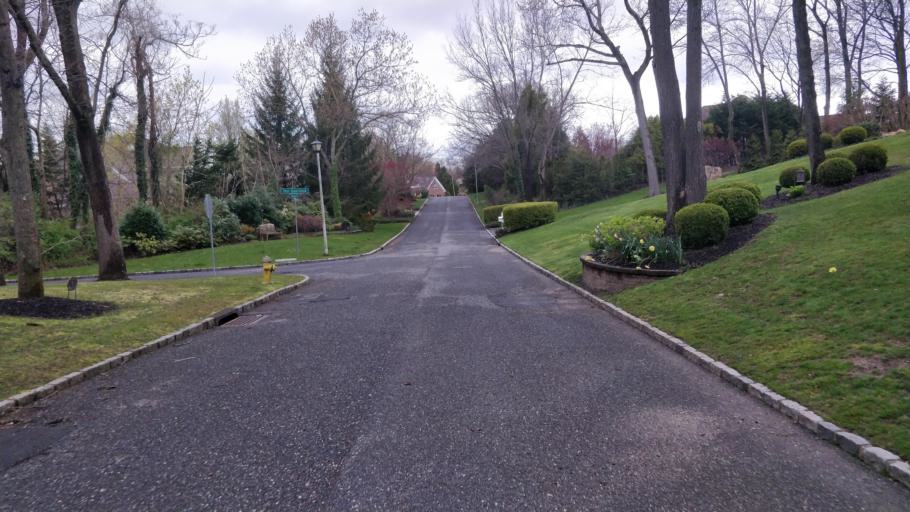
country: US
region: New York
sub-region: Suffolk County
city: East Setauket
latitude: 40.9511
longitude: -73.0906
